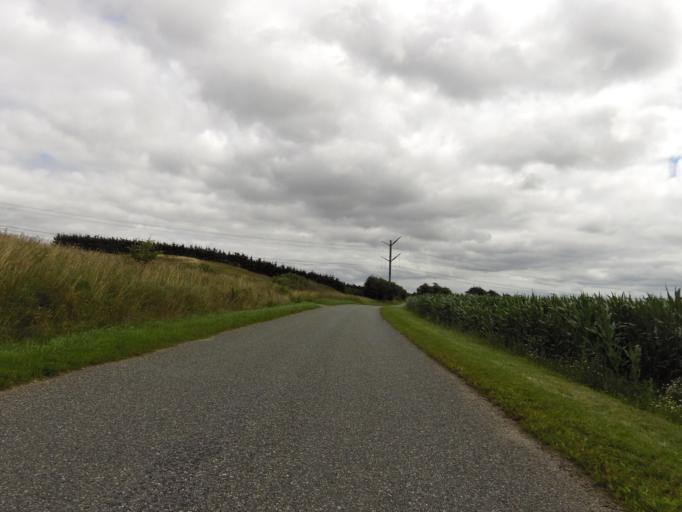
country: DK
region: South Denmark
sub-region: Haderslev Kommune
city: Gram
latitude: 55.3001
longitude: 9.1531
